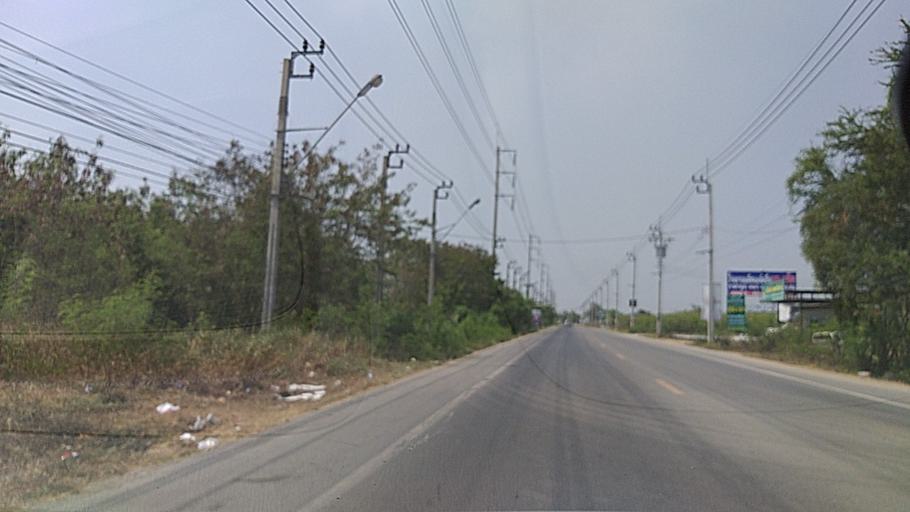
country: TH
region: Nonthaburi
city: Sai Noi
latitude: 13.9261
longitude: 100.3195
